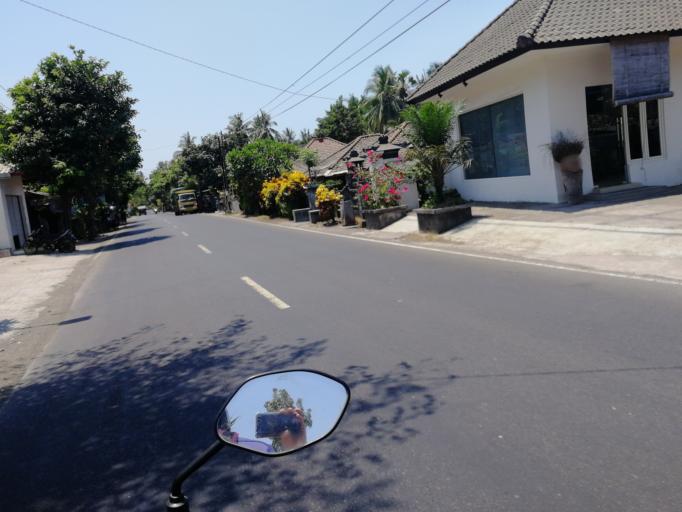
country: ID
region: Bali
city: Banjar Trunyan
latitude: -8.1506
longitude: 115.4109
